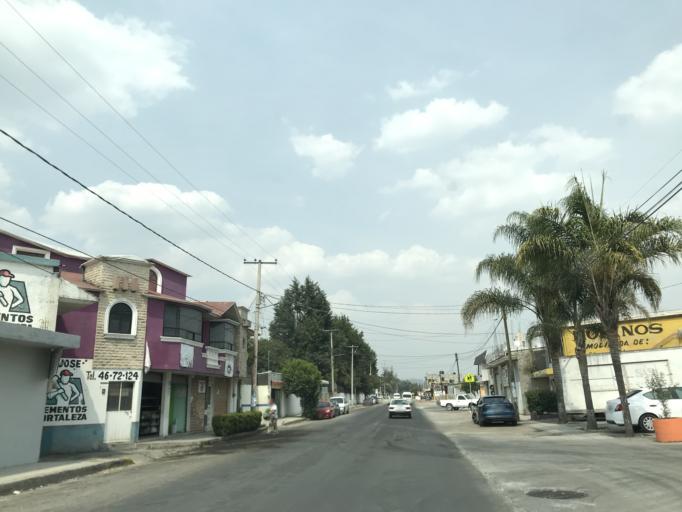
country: MX
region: Tlaxcala
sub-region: Panotla
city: Fraccionamiento la Virgen
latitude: 19.3192
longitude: -98.3104
